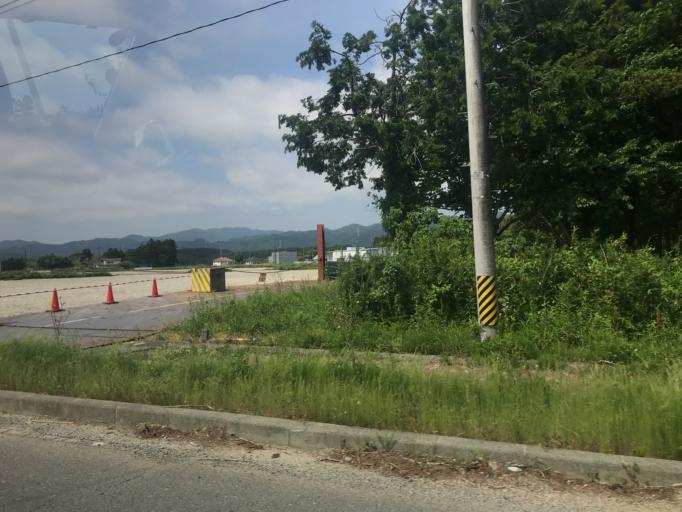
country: JP
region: Fukushima
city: Namie
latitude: 37.3534
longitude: 141.0001
